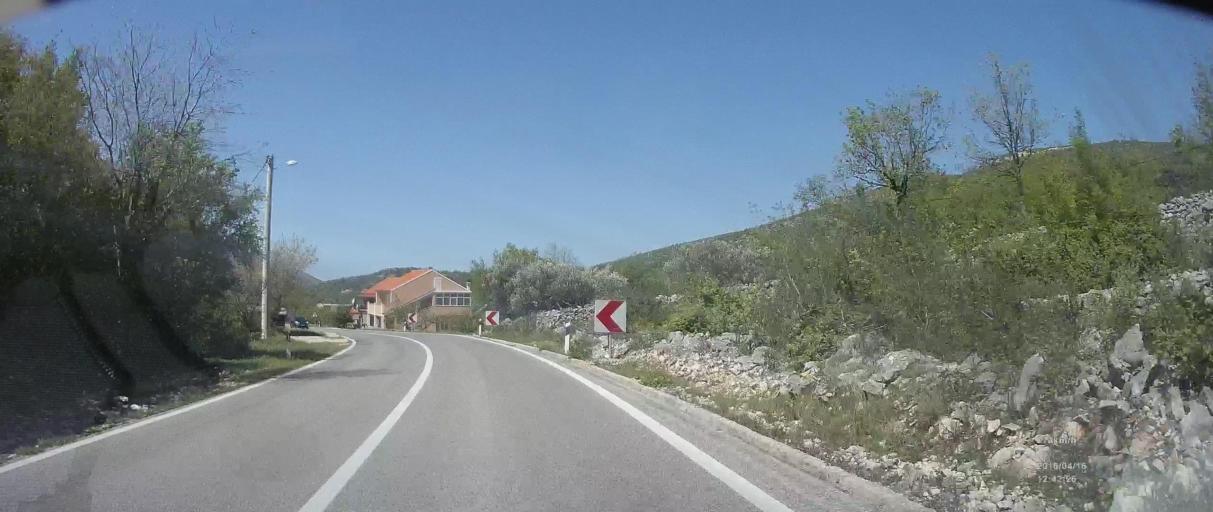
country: HR
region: Sibensko-Kniniska
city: Rogoznica
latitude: 43.6292
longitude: 16.0896
